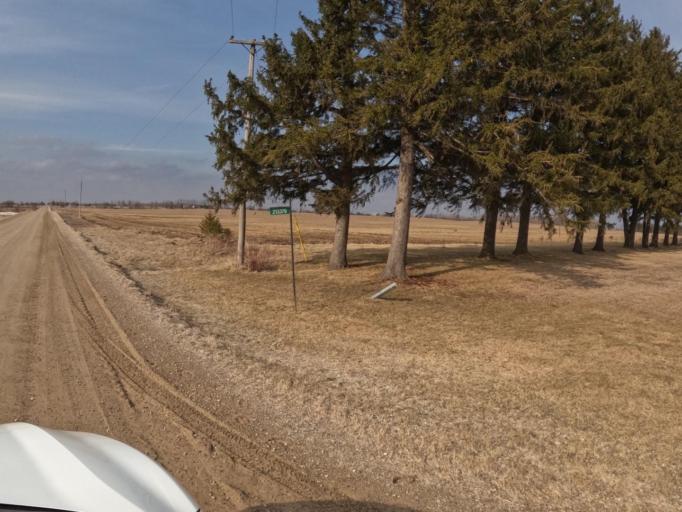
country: CA
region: Ontario
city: Shelburne
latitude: 43.9142
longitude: -80.2881
